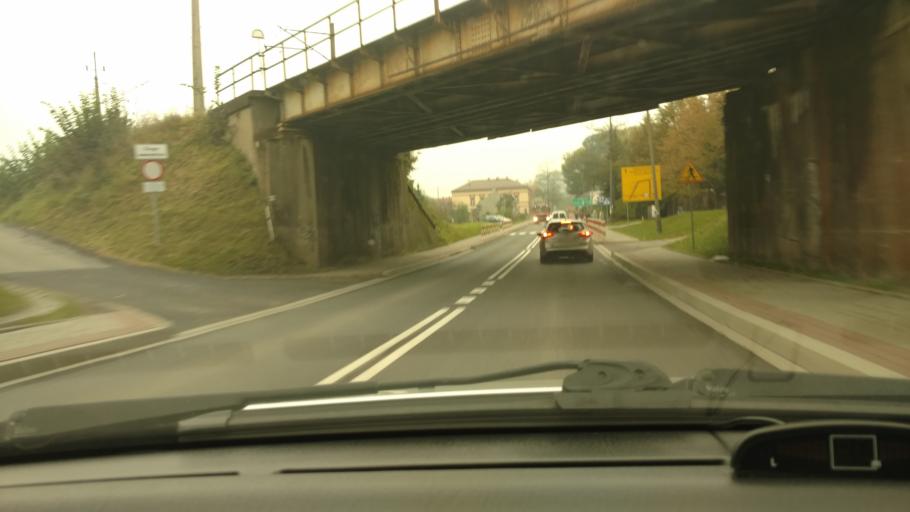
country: PL
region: Lesser Poland Voivodeship
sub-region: Powiat nowosadecki
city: Grybow
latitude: 49.6229
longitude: 20.9526
